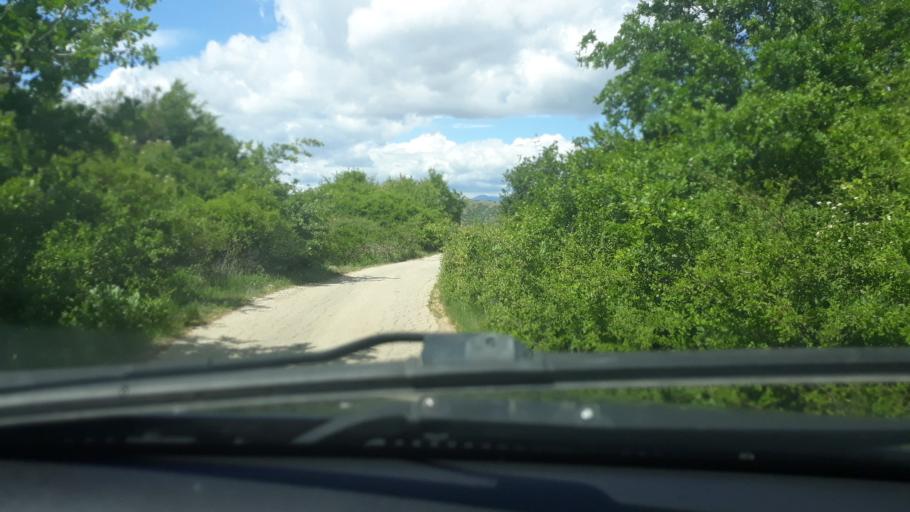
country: MK
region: Krivogastani
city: Krivogashtani
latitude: 41.3307
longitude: 21.3023
